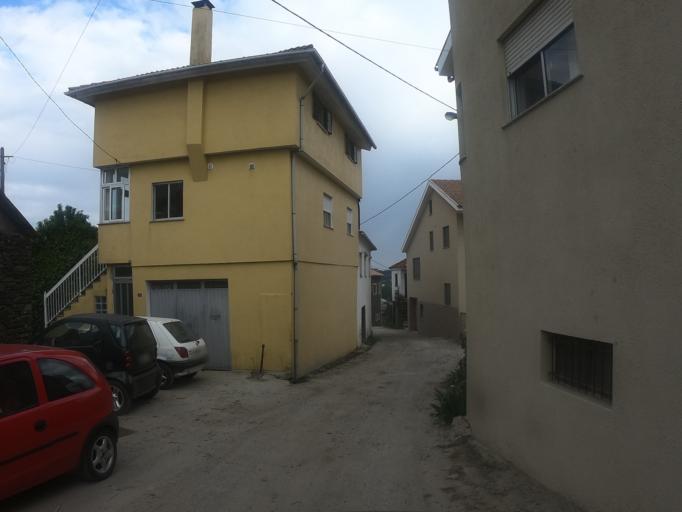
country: PT
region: Vila Real
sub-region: Santa Marta de Penaguiao
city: Santa Marta de Penaguiao
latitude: 41.3042
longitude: -7.8786
